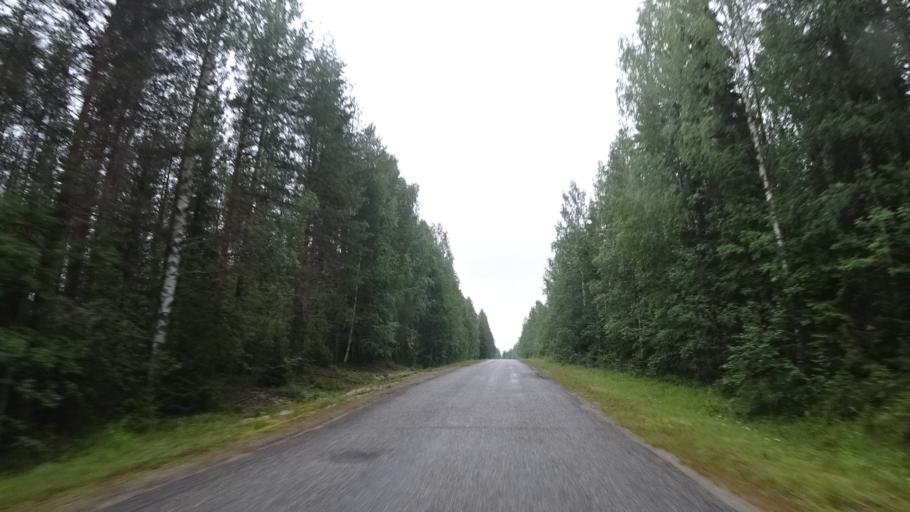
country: FI
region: North Karelia
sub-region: Joensuu
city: Ilomantsi
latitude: 63.2282
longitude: 30.8208
